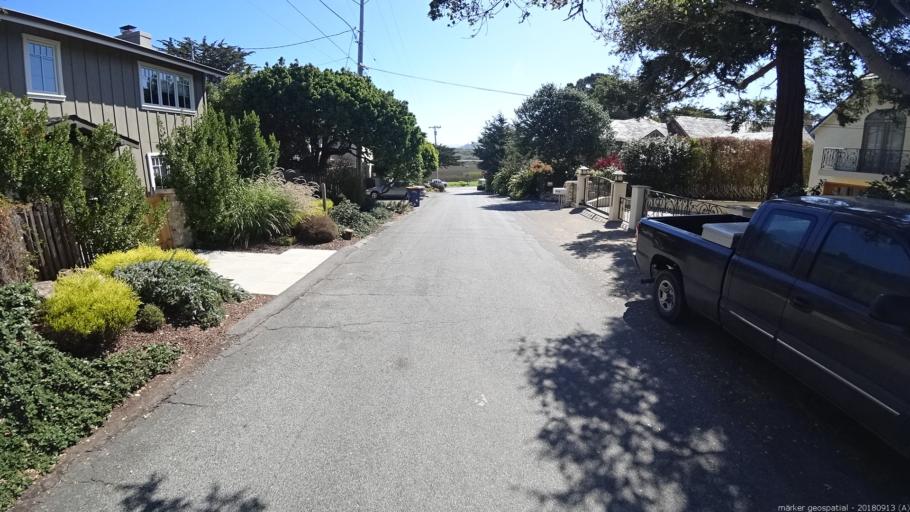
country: US
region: California
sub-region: Monterey County
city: Carmel-by-the-Sea
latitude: 36.5404
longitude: -121.9293
